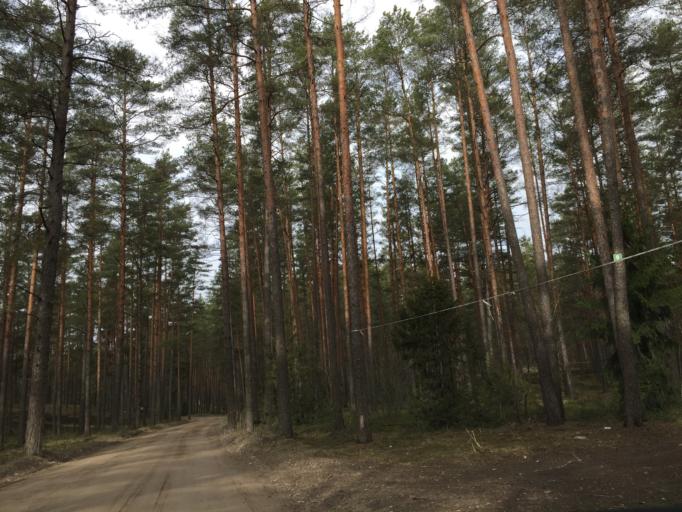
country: LV
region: Garkalne
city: Garkalne
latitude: 57.0680
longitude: 24.4668
